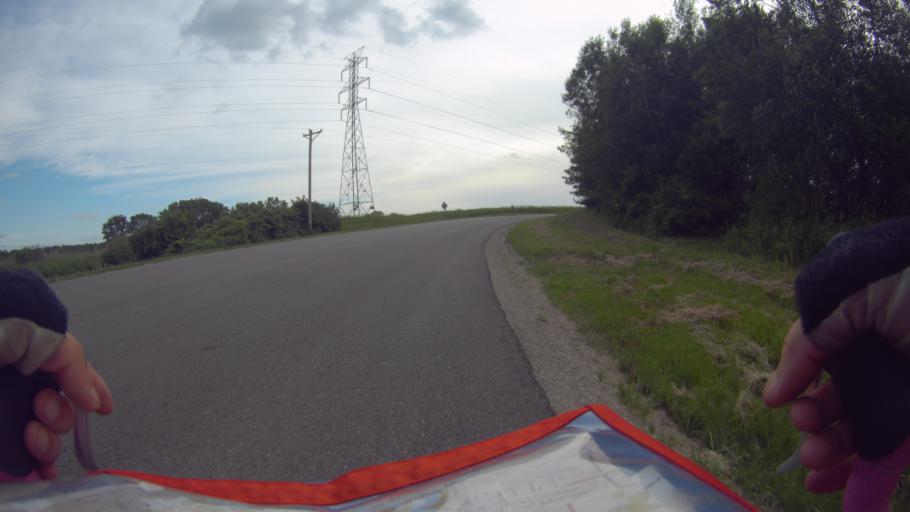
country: US
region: Wisconsin
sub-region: Dane County
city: Oregon
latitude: 42.9823
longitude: -89.3639
